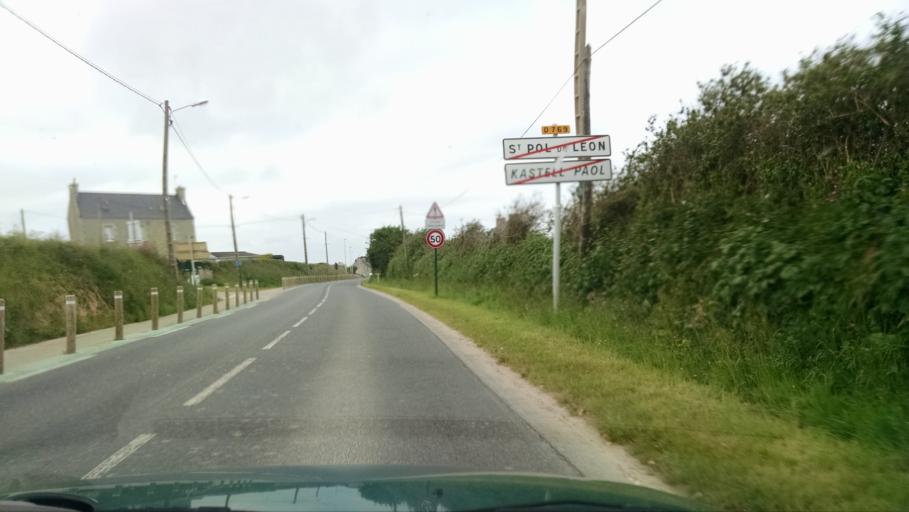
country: FR
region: Brittany
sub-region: Departement du Finistere
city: Saint-Pol-de-Leon
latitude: 48.6912
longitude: -3.9891
